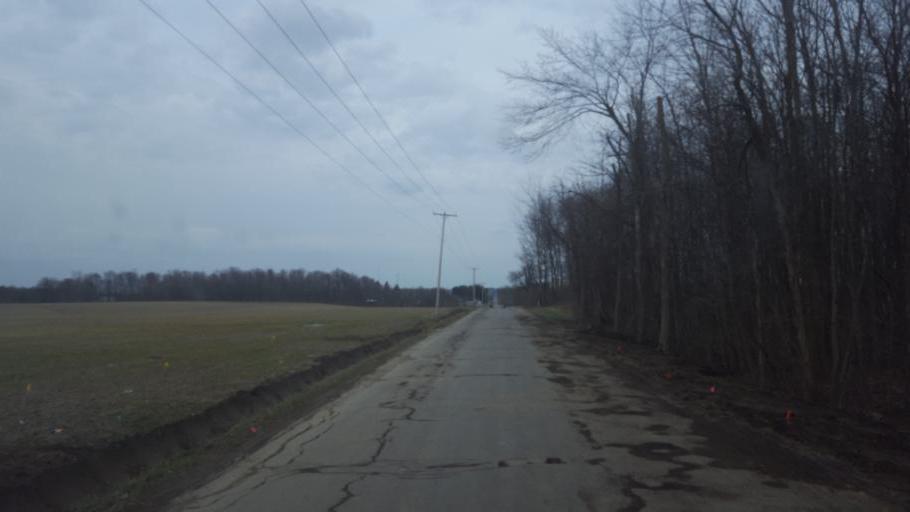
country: US
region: Ohio
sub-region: Richland County
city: Lexington
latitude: 40.5864
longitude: -82.6135
